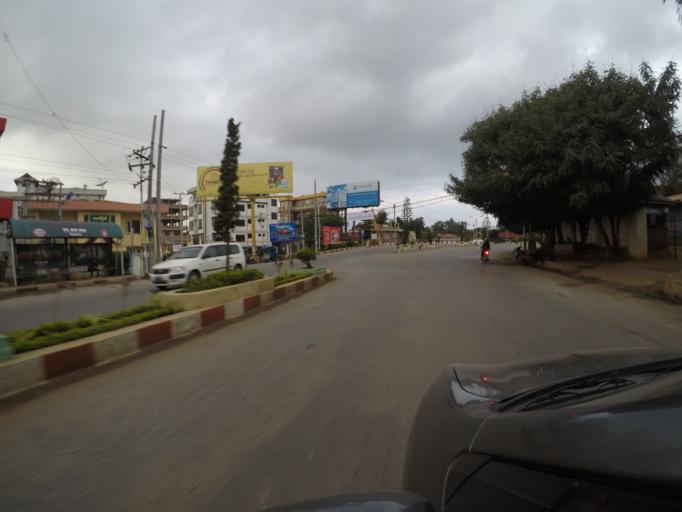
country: MM
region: Shan
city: Taunggyi
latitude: 20.8001
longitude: 97.0365
